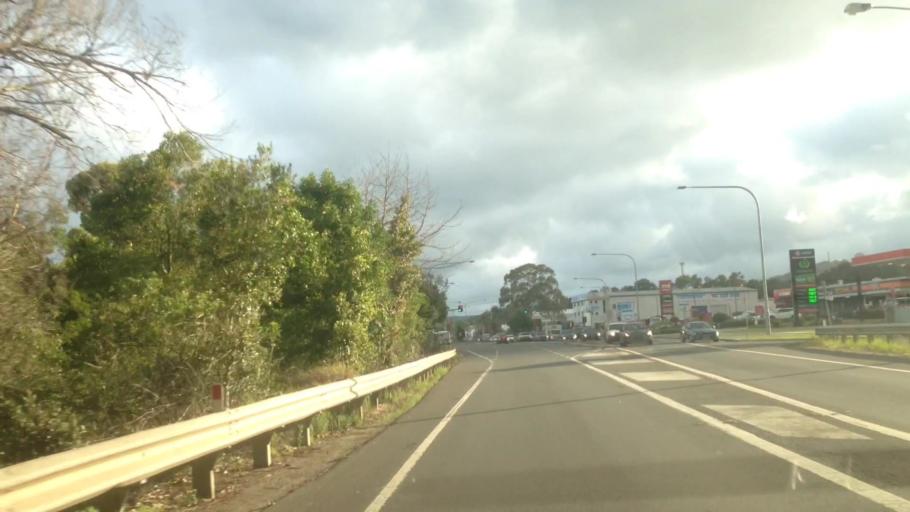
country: AU
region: New South Wales
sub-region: Wyong Shire
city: Chittaway Bay
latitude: -33.2932
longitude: 151.4232
